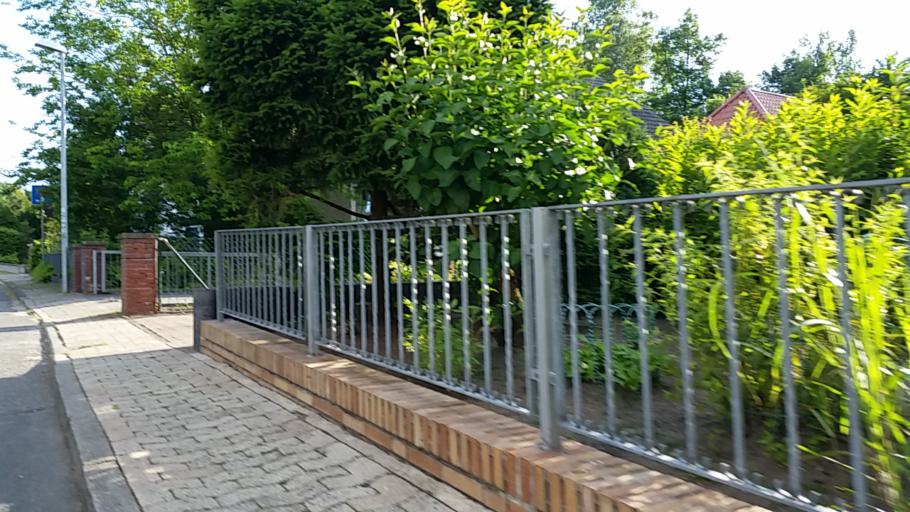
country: DE
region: Lower Saxony
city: Lehre
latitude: 52.3897
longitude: 10.7101
